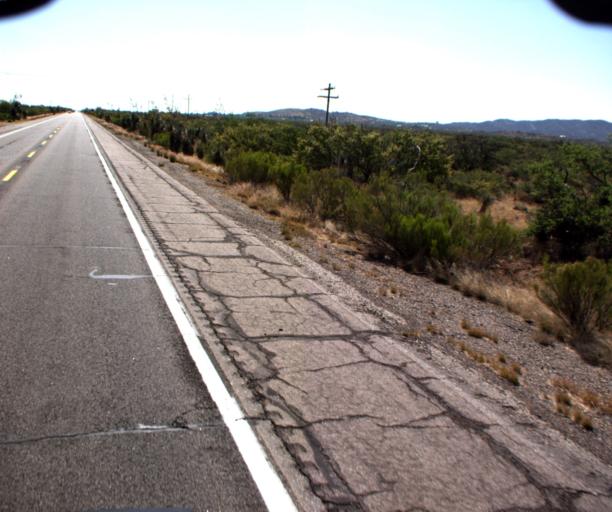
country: US
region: Arizona
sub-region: Pinal County
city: Oracle
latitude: 32.6143
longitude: -110.8306
